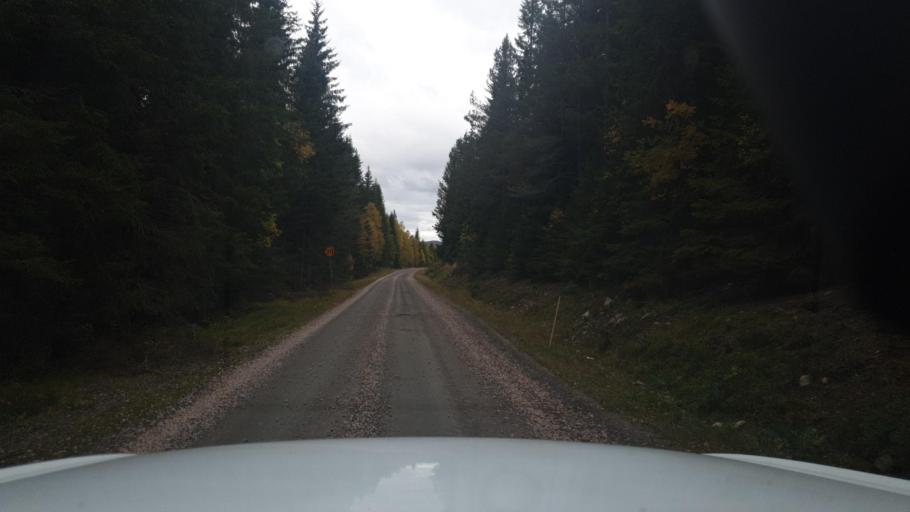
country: SE
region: Vaermland
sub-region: Eda Kommun
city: Charlottenberg
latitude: 60.1289
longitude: 12.5936
